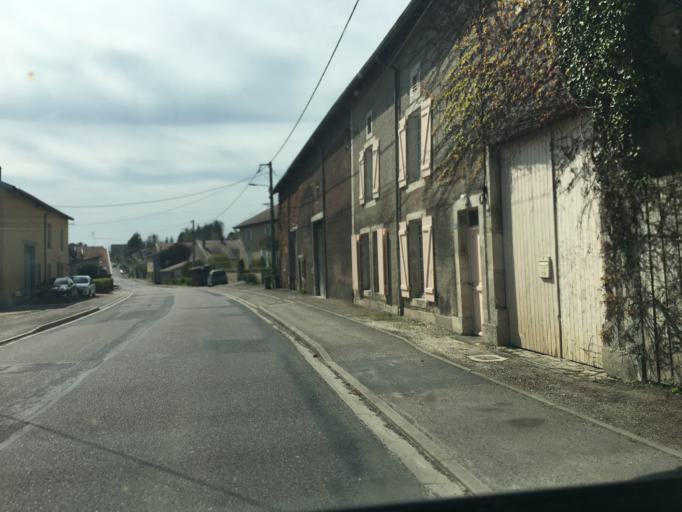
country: FR
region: Lorraine
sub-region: Departement de la Meuse
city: Lerouville
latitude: 48.8315
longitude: 5.5082
